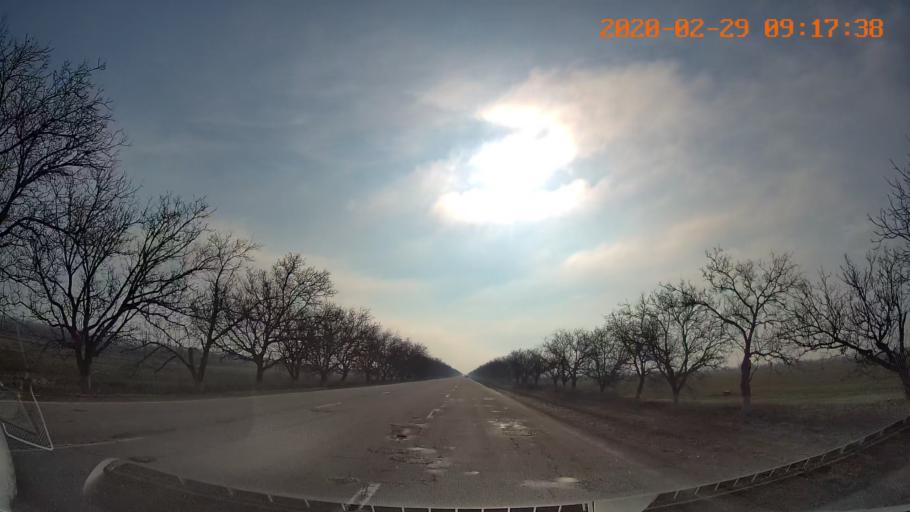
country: MD
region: Telenesti
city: Pervomaisc
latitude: 46.7811
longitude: 29.9079
